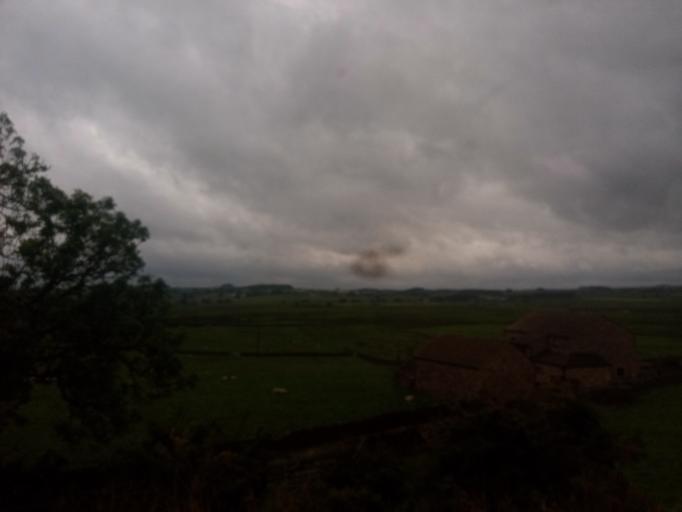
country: GB
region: England
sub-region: North Yorkshire
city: Settle
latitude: 54.0241
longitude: -2.2668
